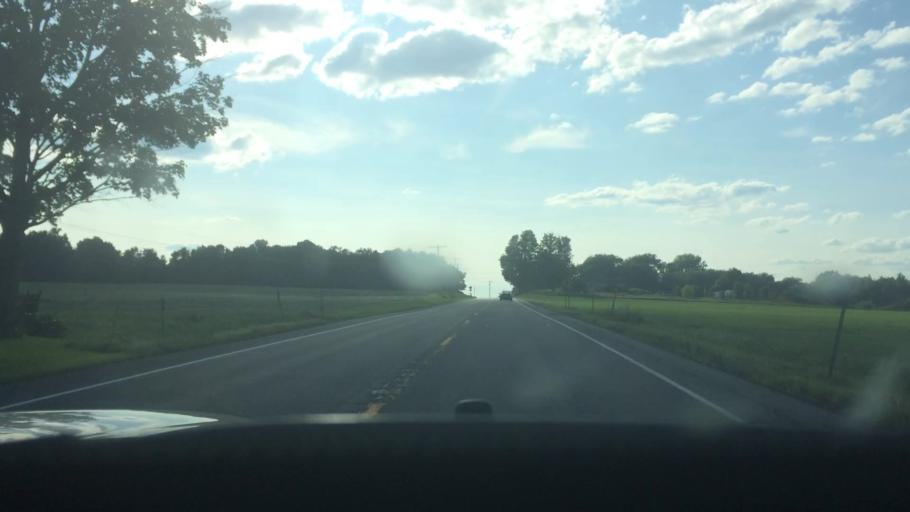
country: US
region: New York
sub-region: St. Lawrence County
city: Potsdam
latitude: 44.6897
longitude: -74.7413
